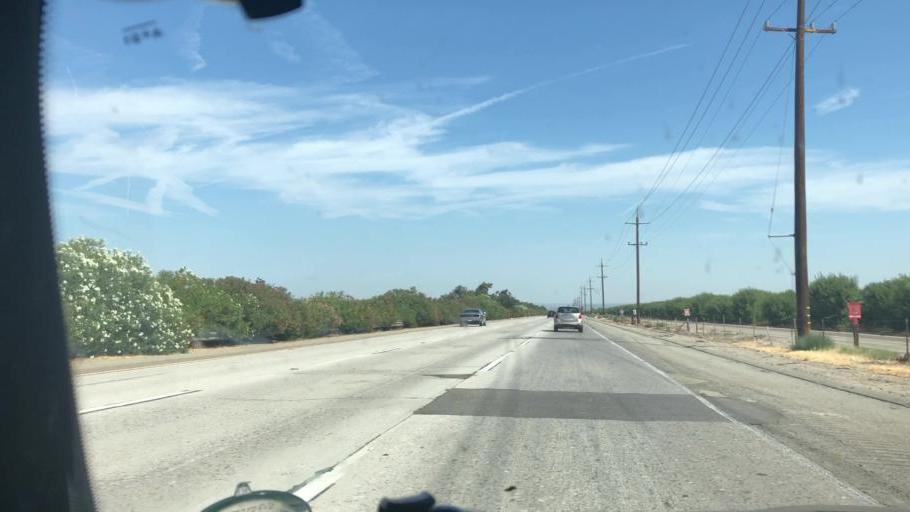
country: US
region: California
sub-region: Kern County
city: Weedpatch
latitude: 35.0347
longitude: -118.9604
